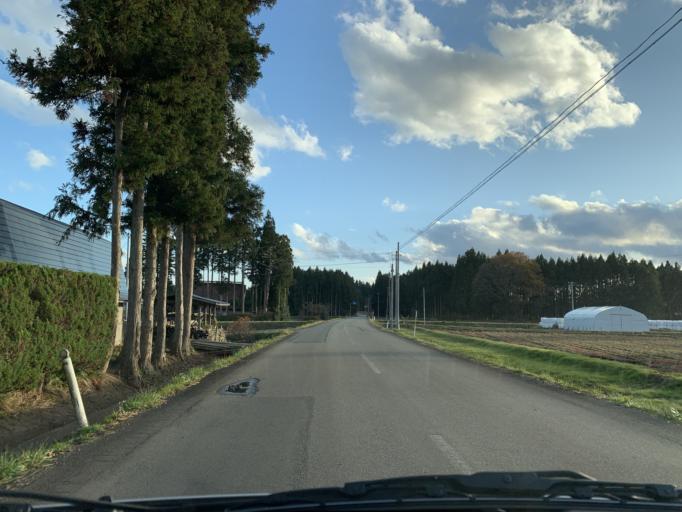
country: JP
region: Iwate
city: Mizusawa
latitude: 39.1223
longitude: 141.0366
